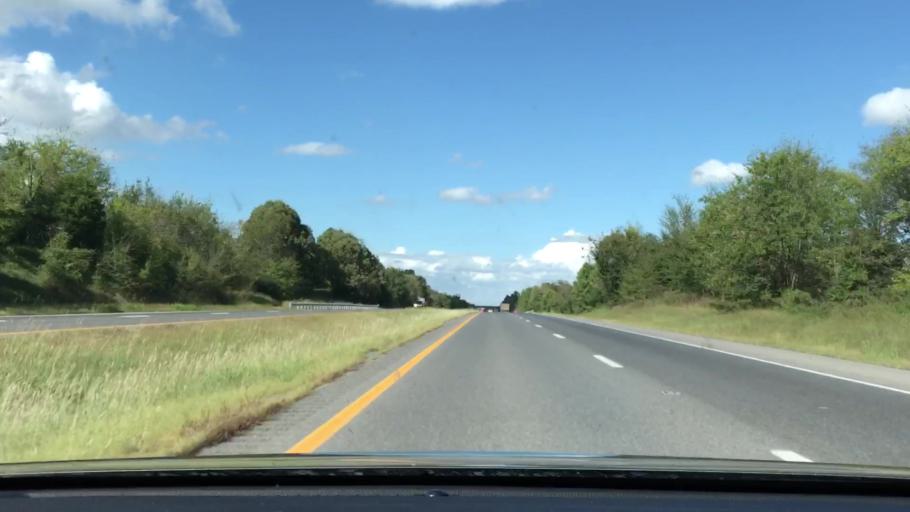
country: US
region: Kentucky
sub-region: Marshall County
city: Calvert City
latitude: 36.9580
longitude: -88.3490
